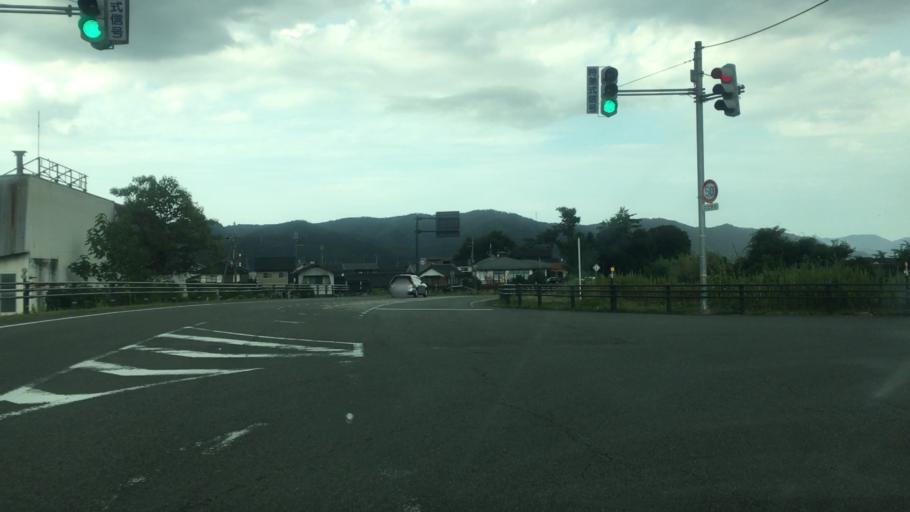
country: JP
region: Hyogo
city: Toyooka
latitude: 35.4773
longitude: 134.7864
